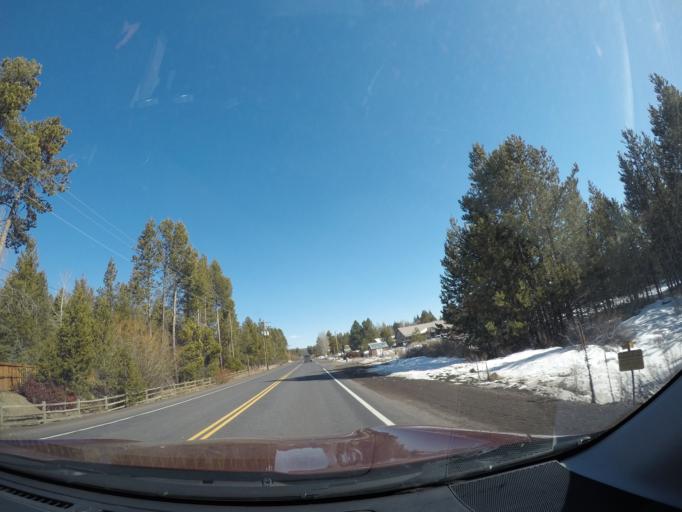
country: US
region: Oregon
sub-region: Deschutes County
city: Sunriver
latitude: 43.8630
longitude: -121.4593
